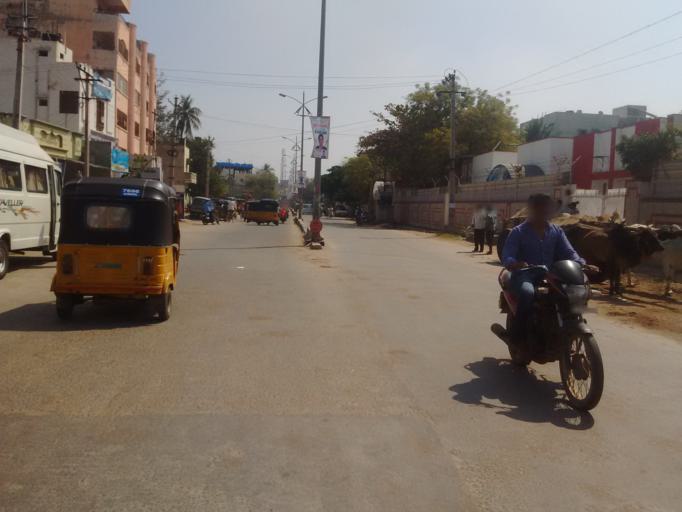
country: IN
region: Telangana
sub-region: Mahbubnagar
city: Alampur
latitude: 15.8408
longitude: 78.0356
